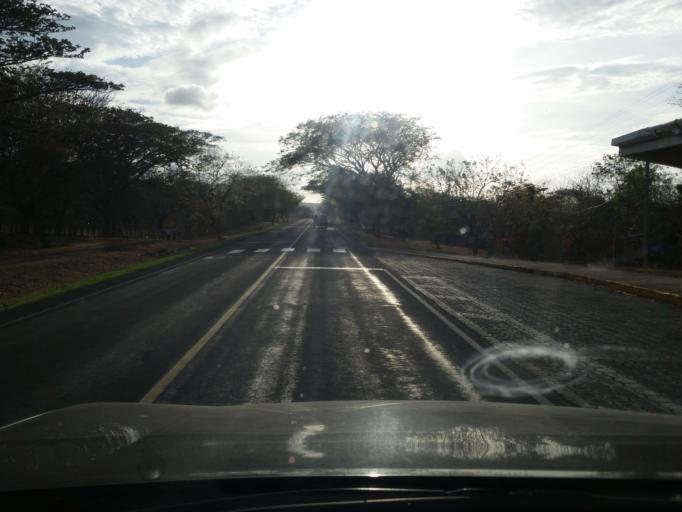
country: NI
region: Rivas
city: Belen
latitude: 11.6008
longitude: -85.9212
